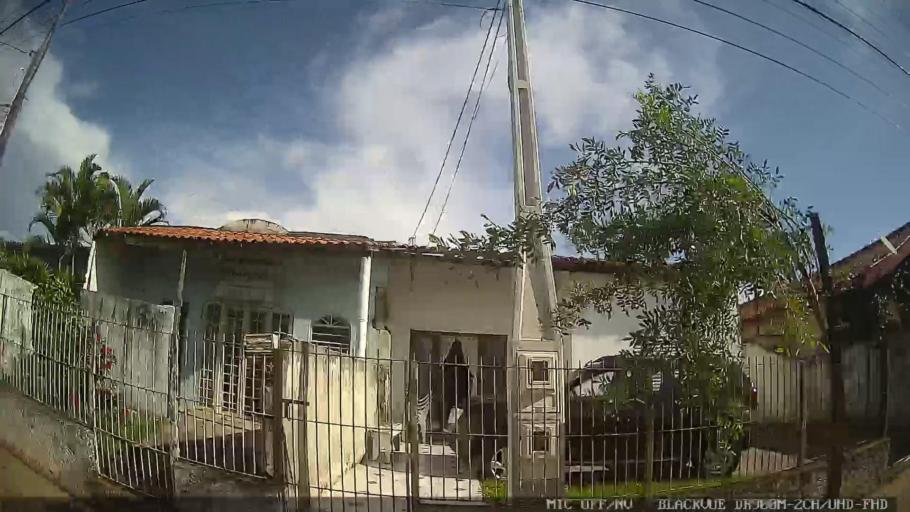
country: BR
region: Sao Paulo
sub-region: Laranjal Paulista
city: Laranjal Paulista
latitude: -23.0852
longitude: -47.7917
